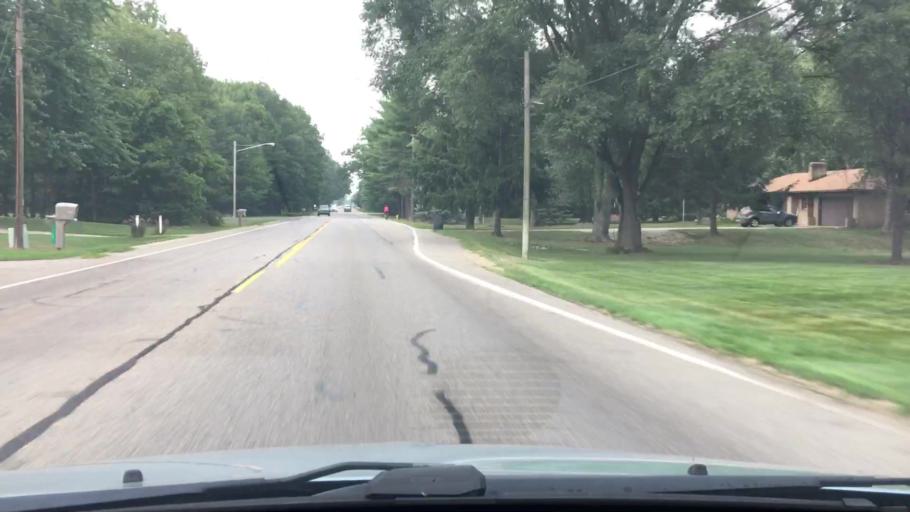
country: US
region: Michigan
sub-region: Ottawa County
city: Hudsonville
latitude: 42.8987
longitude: -85.9018
